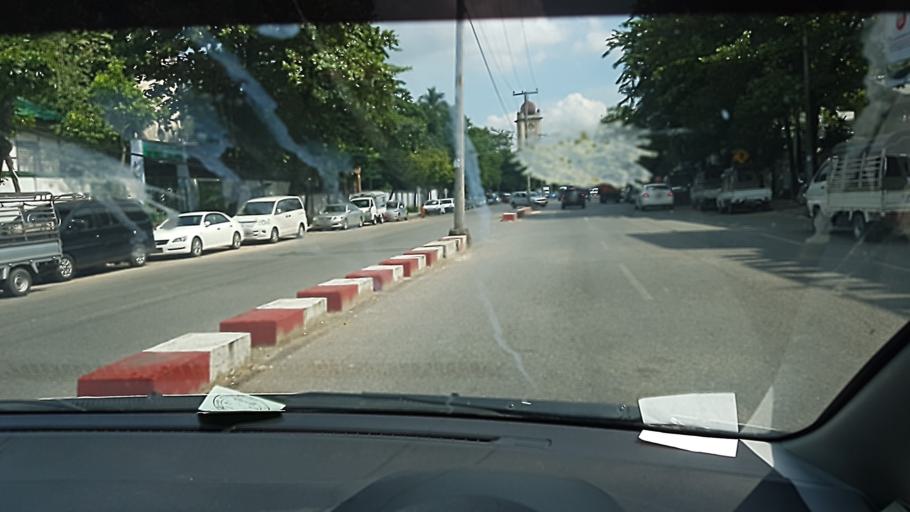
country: MM
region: Yangon
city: Yangon
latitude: 16.8003
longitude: 96.1732
